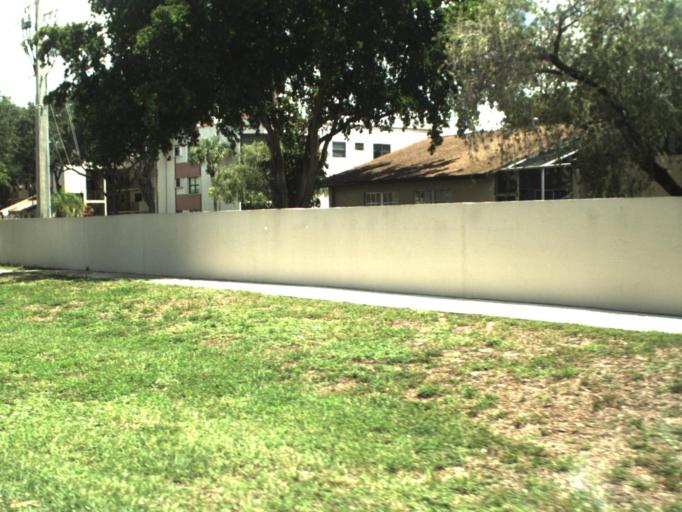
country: US
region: Florida
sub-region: Miami-Dade County
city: Lake Lucerne
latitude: 25.9808
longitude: -80.2684
